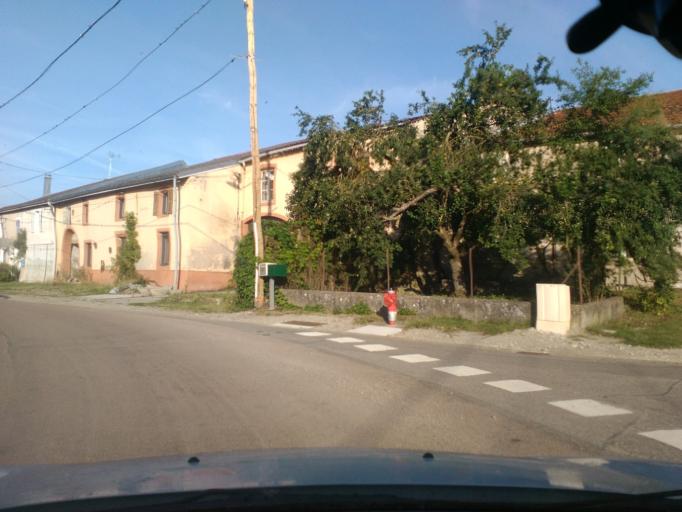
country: FR
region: Lorraine
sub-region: Departement des Vosges
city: Mirecourt
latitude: 48.2803
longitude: 6.0429
